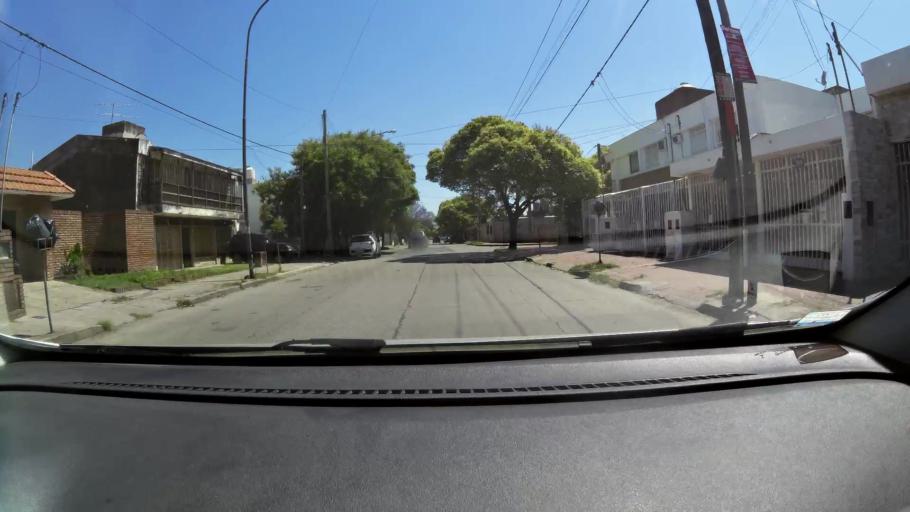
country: AR
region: Cordoba
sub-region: Departamento de Capital
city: Cordoba
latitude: -31.4271
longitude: -64.2102
